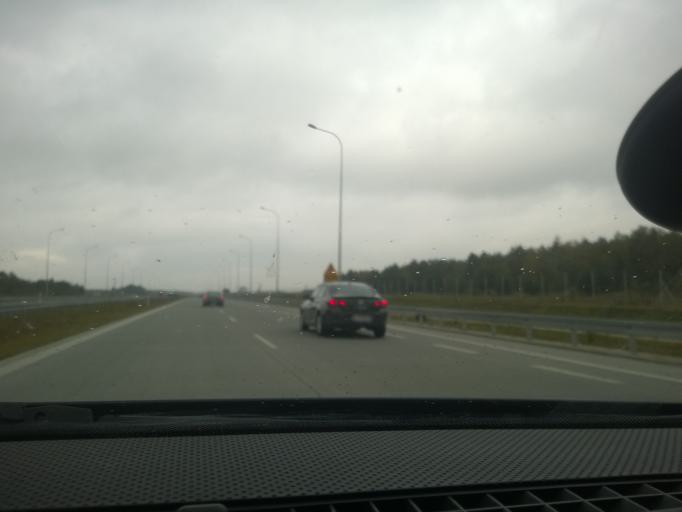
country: PL
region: Lodz Voivodeship
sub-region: Powiat lodzki wschodni
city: Andrespol
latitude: 51.7001
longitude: 19.6027
